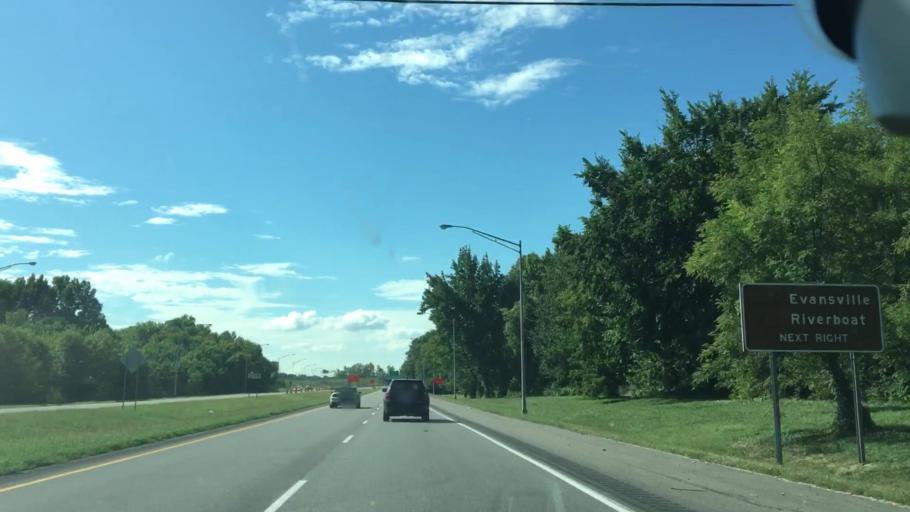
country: US
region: Indiana
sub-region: Vanderburgh County
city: Evansville
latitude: 37.9482
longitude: -87.5433
